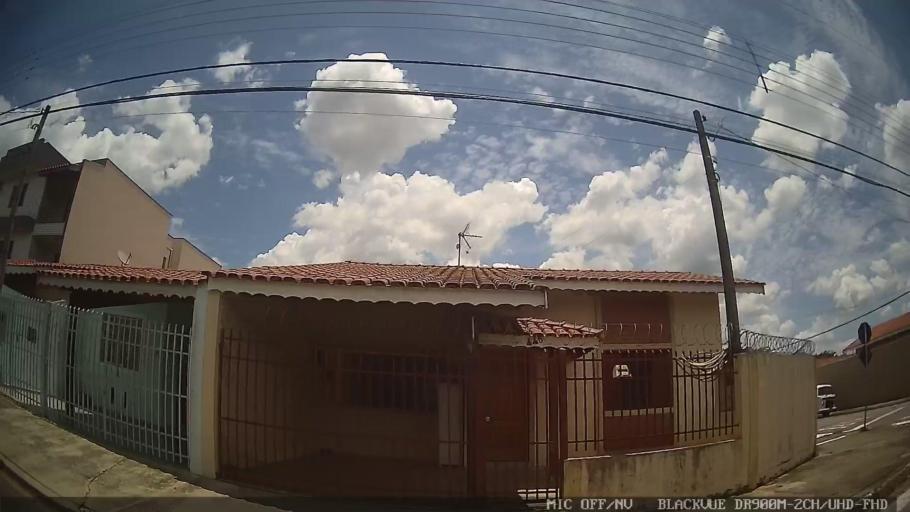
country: BR
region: Sao Paulo
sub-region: Atibaia
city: Atibaia
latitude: -23.1064
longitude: -46.5449
